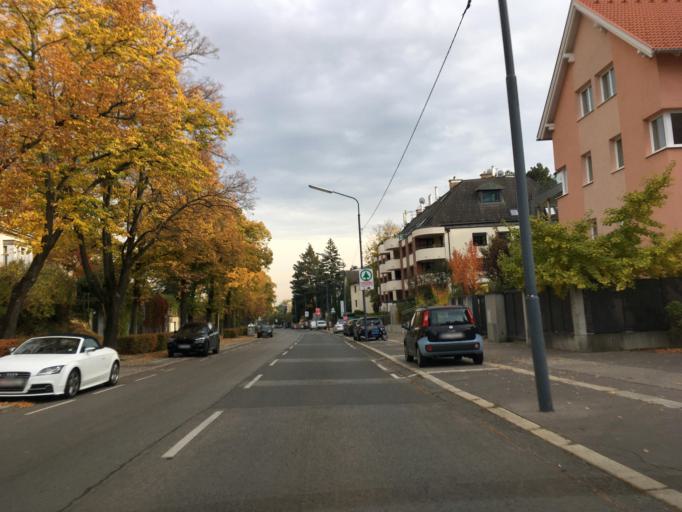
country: AT
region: Lower Austria
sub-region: Politischer Bezirk Wien-Umgebung
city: Klosterneuburg
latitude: 48.2484
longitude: 16.3107
